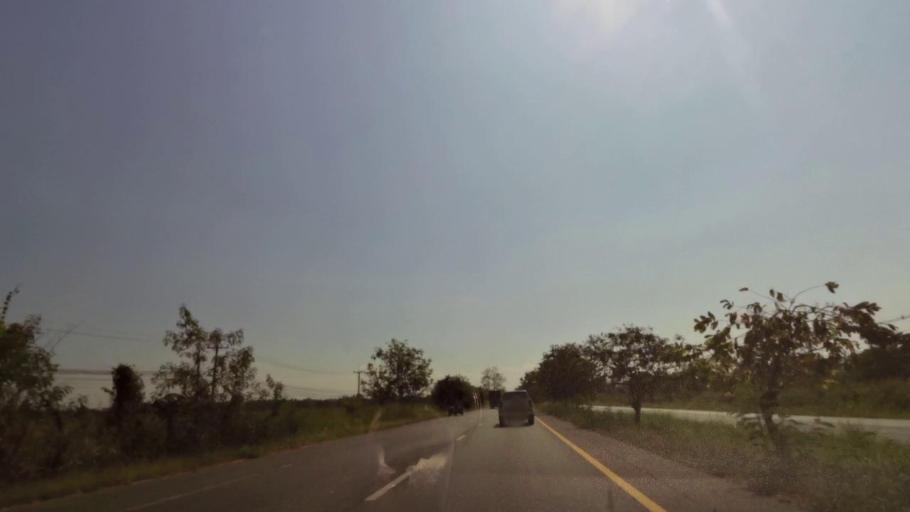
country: TH
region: Nakhon Sawan
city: Kao Liao
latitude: 15.8603
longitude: 100.1168
